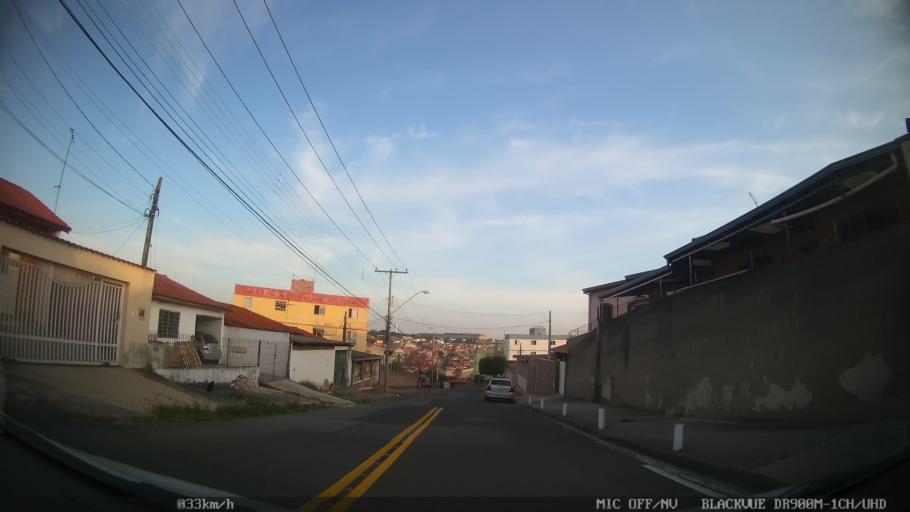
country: BR
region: Sao Paulo
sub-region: Campinas
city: Campinas
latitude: -22.9811
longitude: -47.1330
